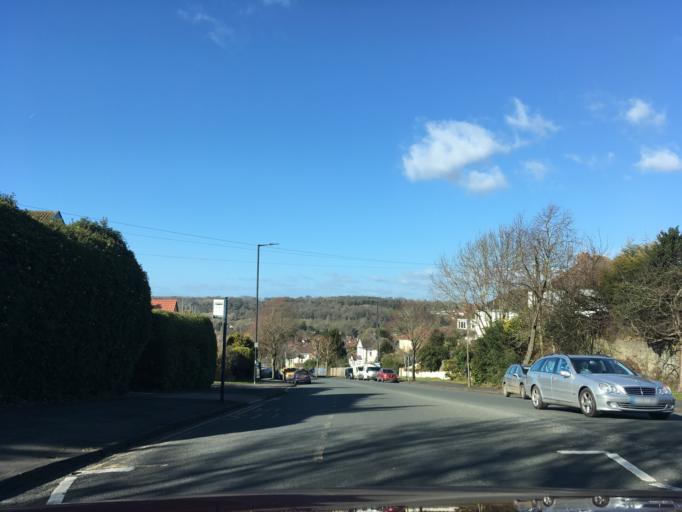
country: GB
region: England
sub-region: Bristol
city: Bristol
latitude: 51.4879
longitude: -2.6174
